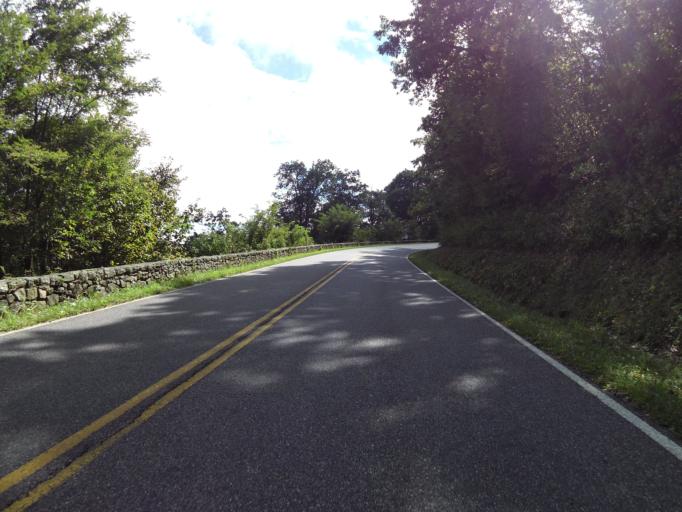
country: US
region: Virginia
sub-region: Page County
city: Luray
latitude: 38.6354
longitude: -78.3190
